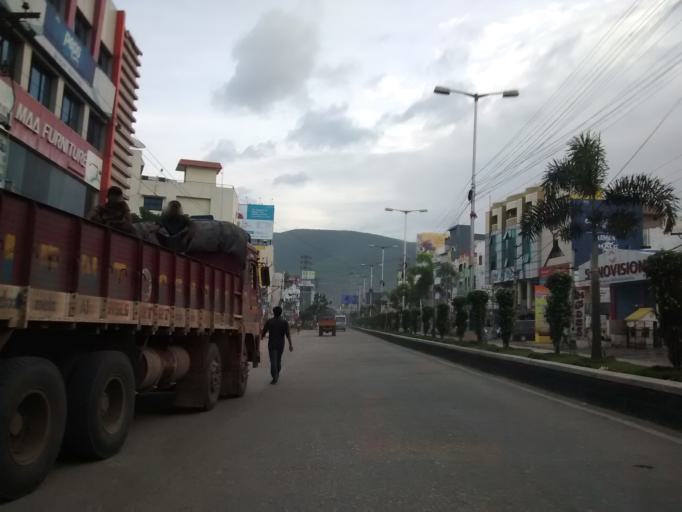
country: IN
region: Andhra Pradesh
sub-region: Chittoor
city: Tirupati
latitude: 13.6396
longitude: 79.4277
